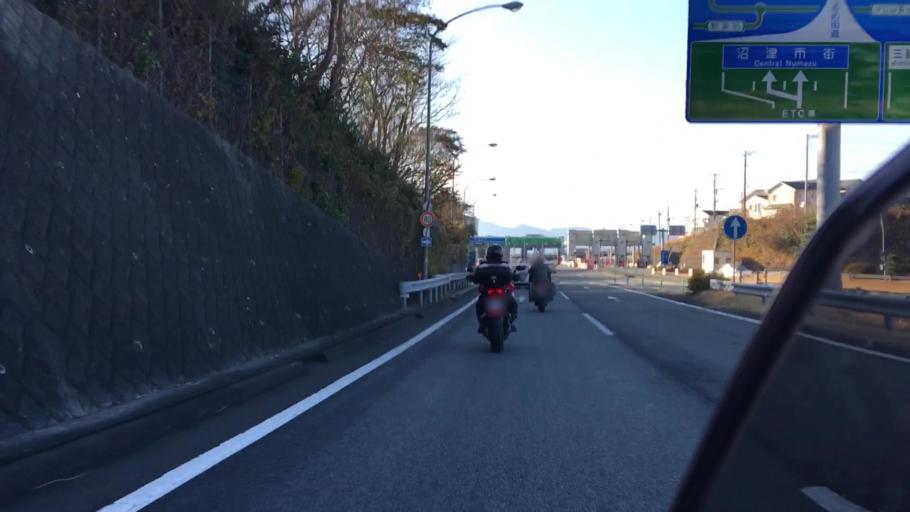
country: JP
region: Shizuoka
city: Numazu
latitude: 35.1468
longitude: 138.8659
